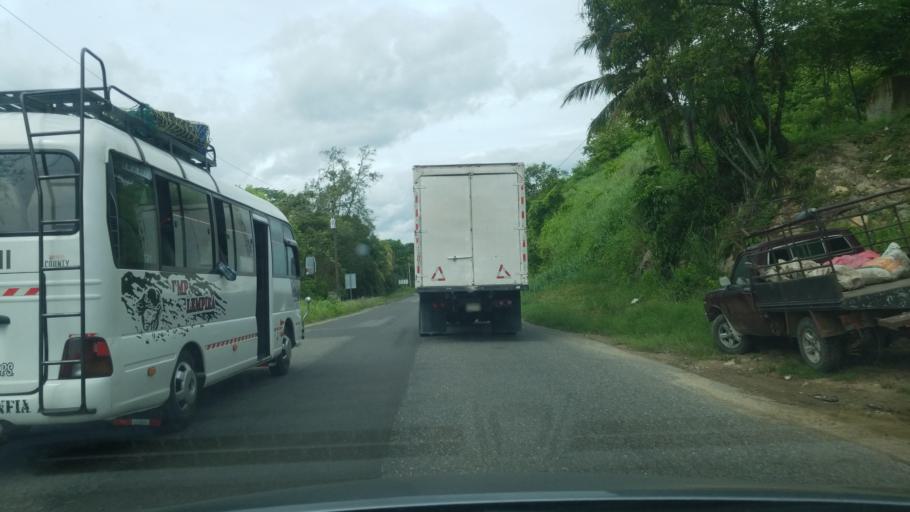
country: HN
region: Santa Barbara
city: San Marcos
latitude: 15.3086
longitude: -88.4402
